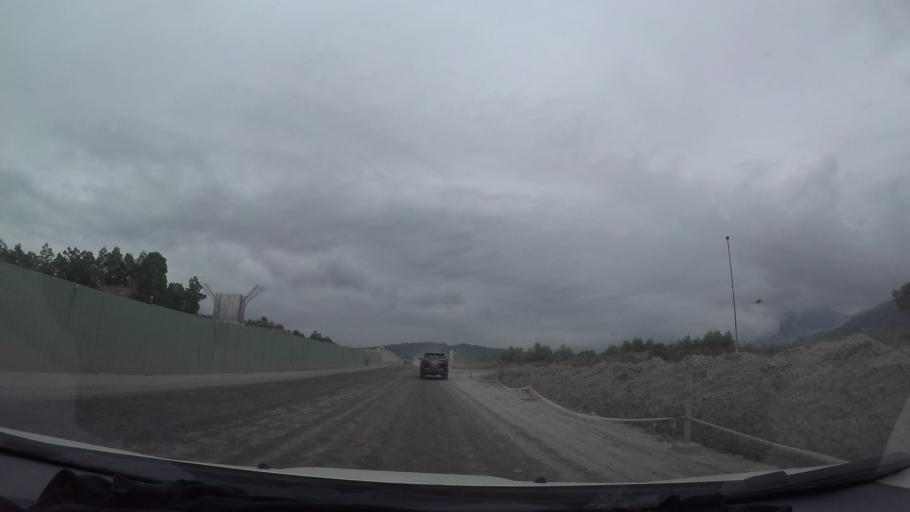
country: VN
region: Da Nang
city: Lien Chieu
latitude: 16.0932
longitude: 108.0870
